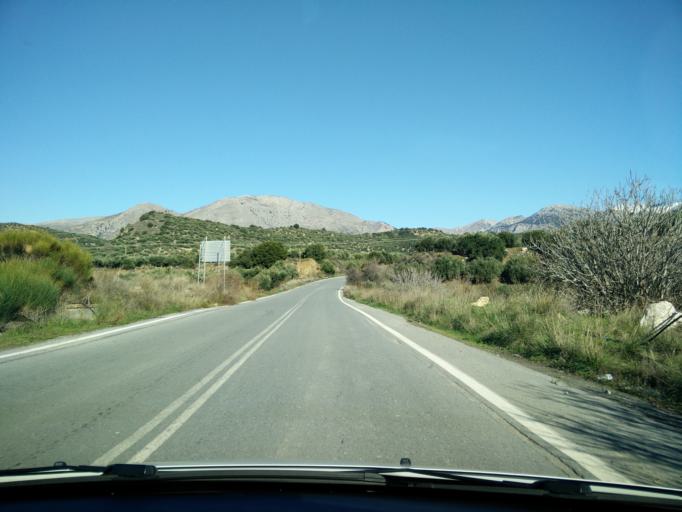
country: GR
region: Crete
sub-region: Nomos Irakleiou
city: Arkalochori
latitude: 35.0773
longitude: 25.3490
